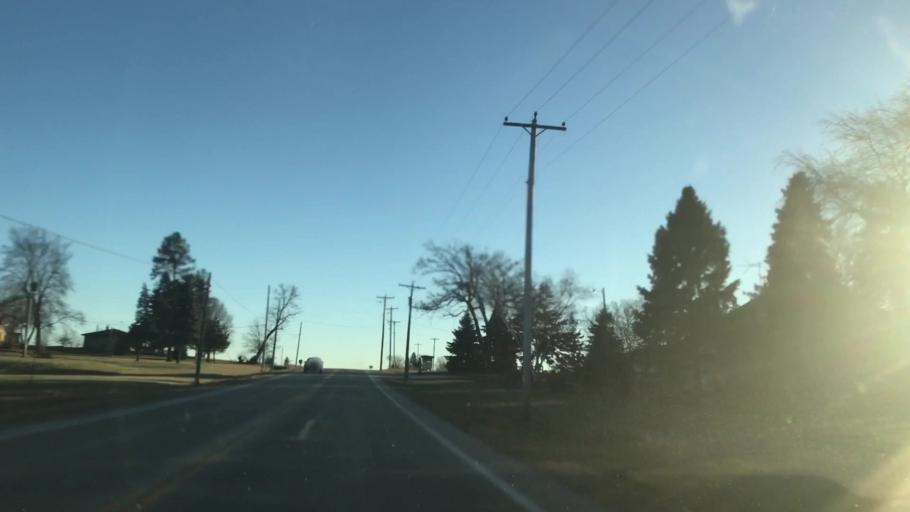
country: US
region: Wisconsin
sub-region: Washington County
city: Richfield
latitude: 43.2895
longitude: -88.1816
